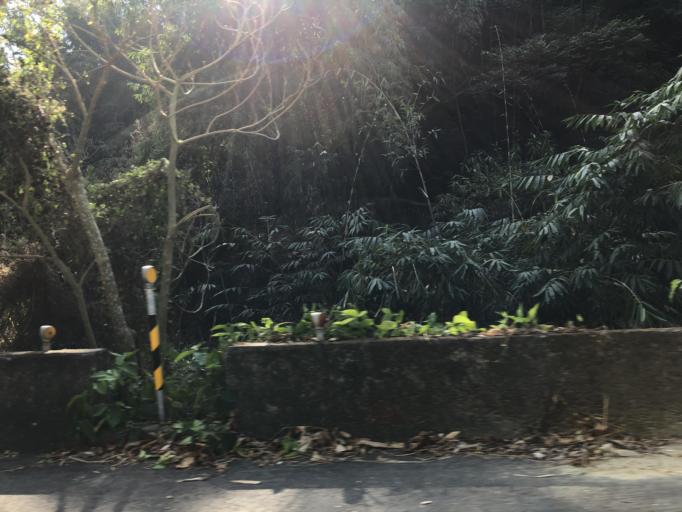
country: TW
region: Taiwan
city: Yujing
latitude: 23.0067
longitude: 120.3903
